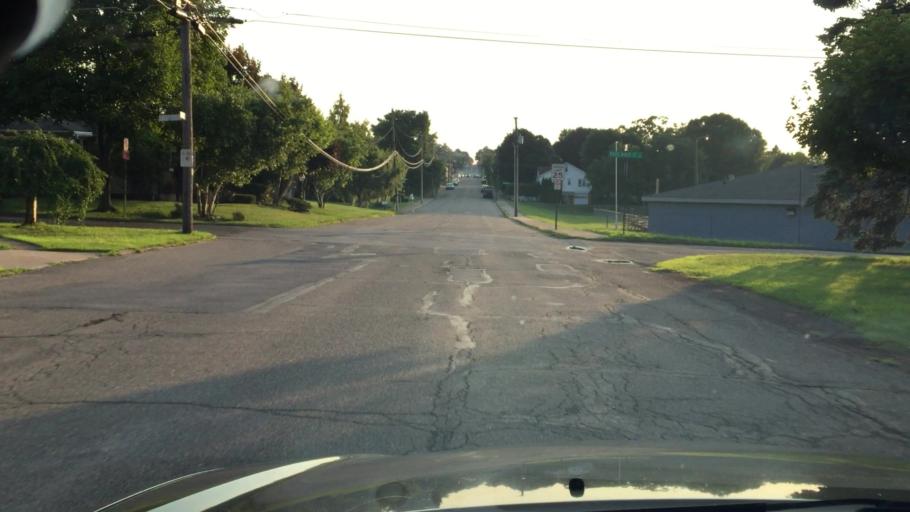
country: US
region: Pennsylvania
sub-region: Luzerne County
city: Harleigh
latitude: 40.9744
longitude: -75.9737
